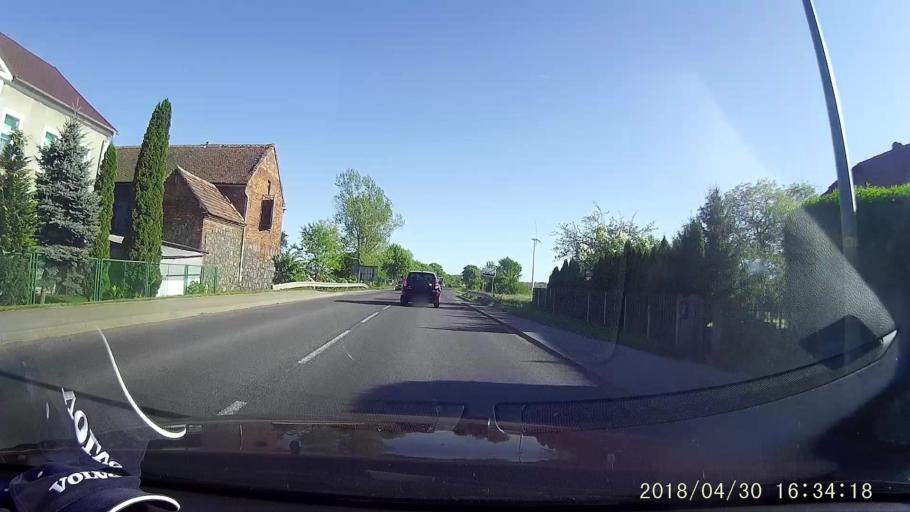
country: PL
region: Lower Silesian Voivodeship
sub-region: Powiat zgorzelecki
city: Sulikow
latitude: 51.0921
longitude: 15.0226
